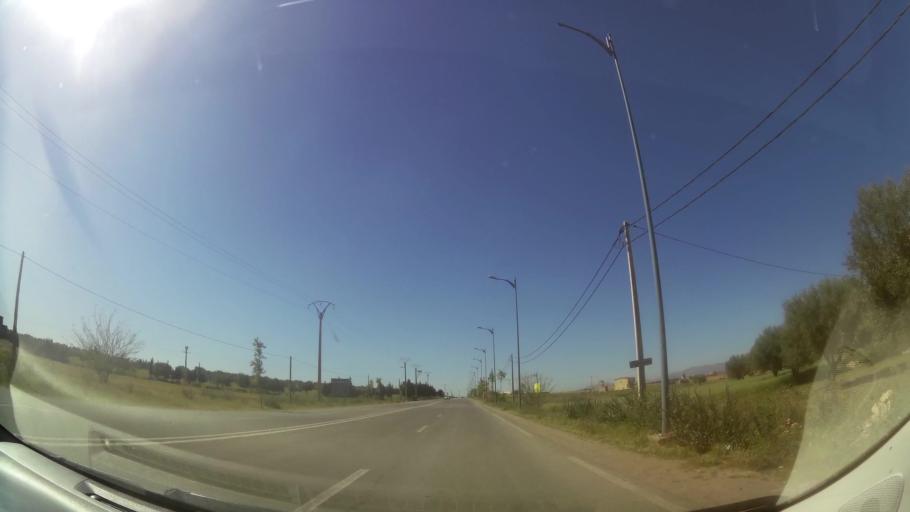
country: MA
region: Oriental
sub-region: Oujda-Angad
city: Oujda
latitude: 34.7214
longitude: -1.8660
